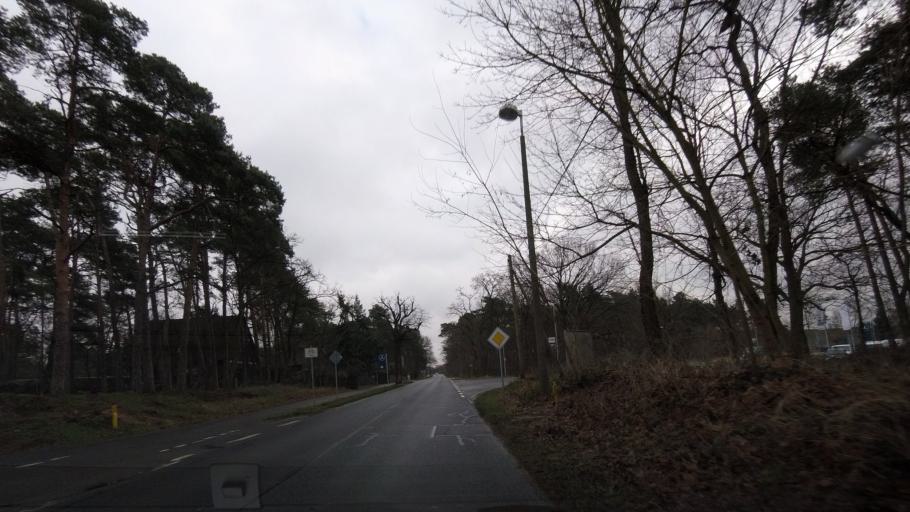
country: DE
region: Brandenburg
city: Luckenwalde
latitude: 52.0988
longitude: 13.1379
